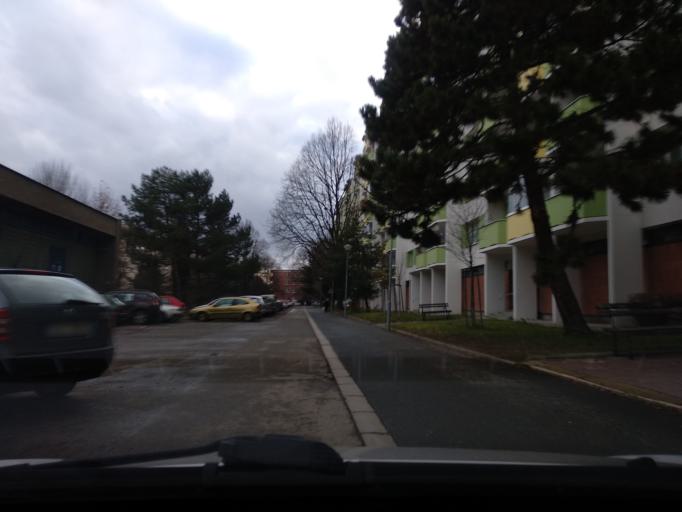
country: CZ
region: South Moravian
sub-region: Mesto Brno
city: Brno
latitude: 49.2266
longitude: 16.6215
